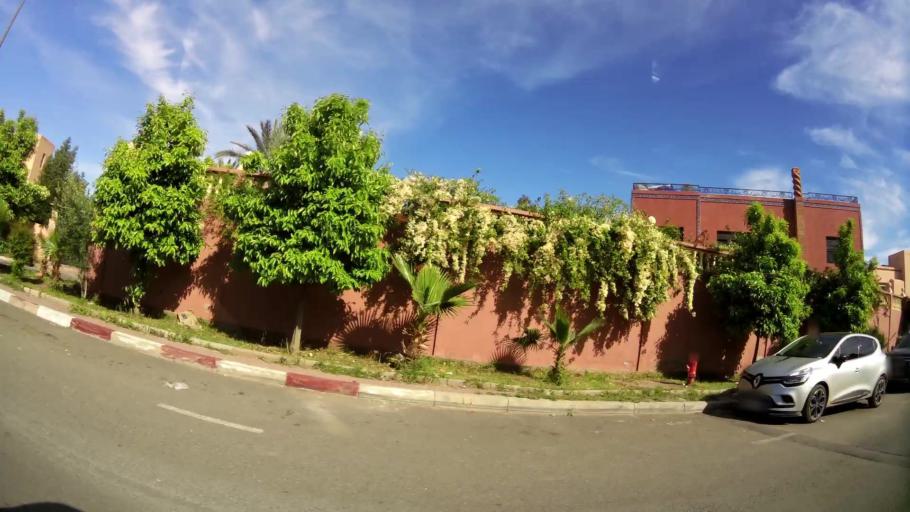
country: MA
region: Marrakech-Tensift-Al Haouz
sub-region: Marrakech
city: Marrakesh
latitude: 31.6503
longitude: -8.0416
